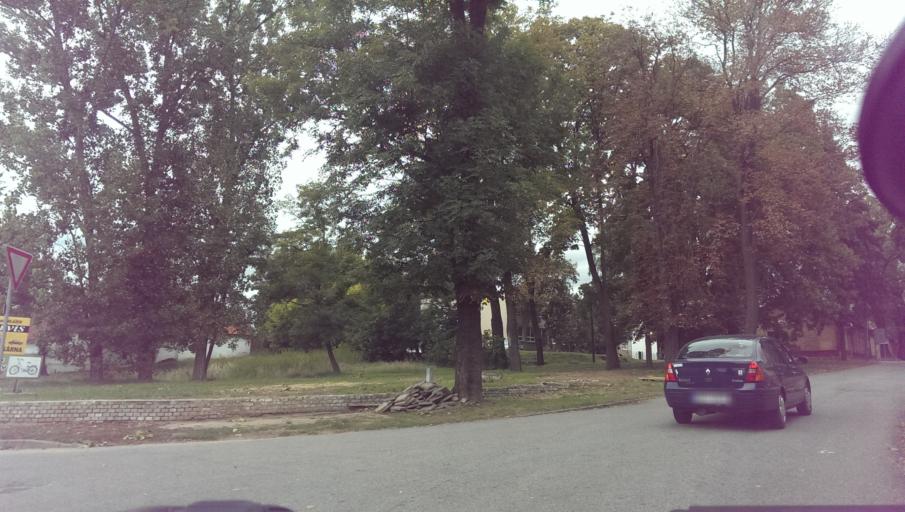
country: CZ
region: South Moravian
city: Bzenec
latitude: 48.9705
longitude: 17.2809
